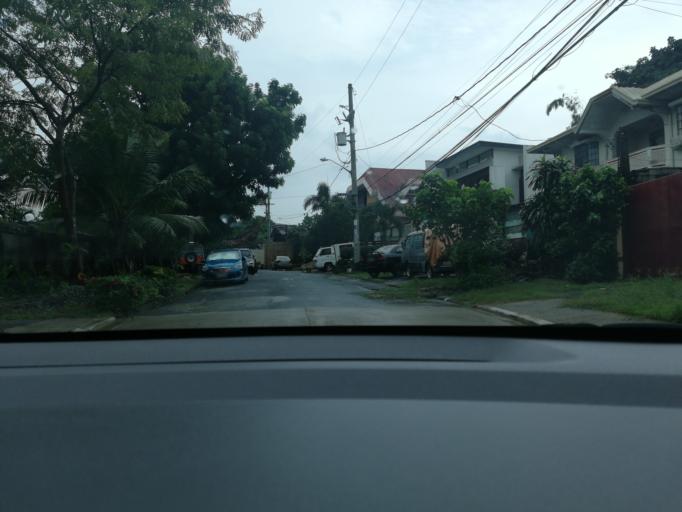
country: PH
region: Metro Manila
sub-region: Quezon City
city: Quezon City
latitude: 14.6801
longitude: 121.0778
